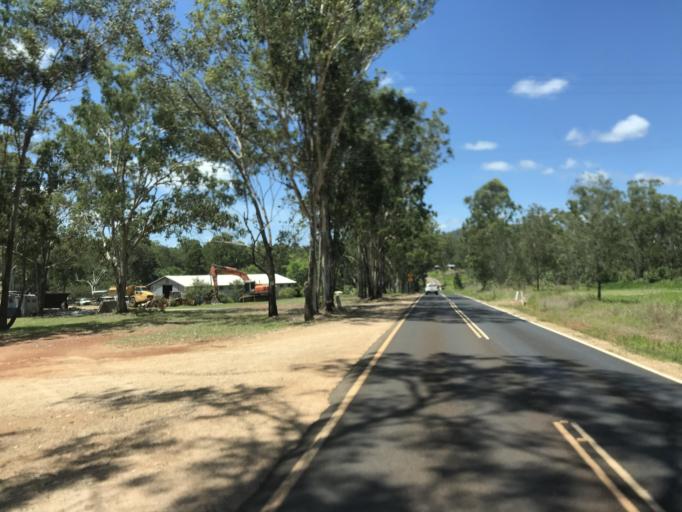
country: AU
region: Queensland
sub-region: Tablelands
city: Atherton
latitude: -17.4162
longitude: 145.3926
